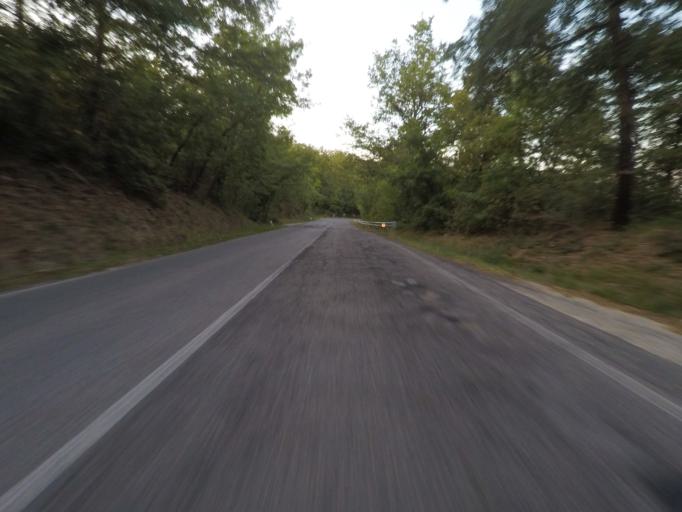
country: IT
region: Tuscany
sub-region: Provincia di Siena
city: Torrita di Siena
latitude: 43.1432
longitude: 11.7353
